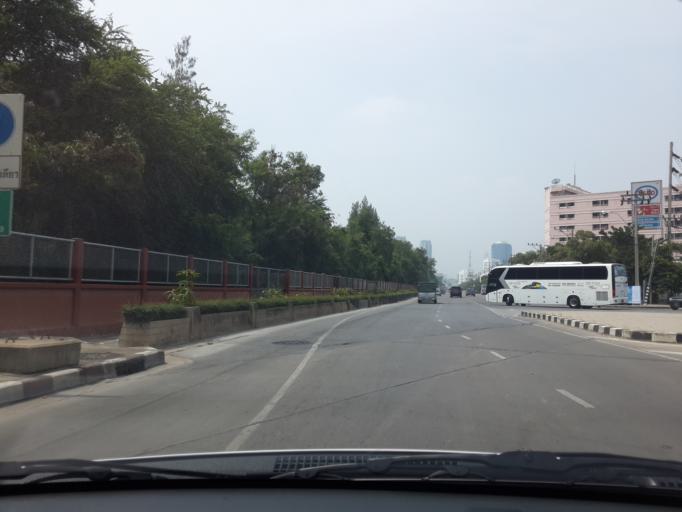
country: TH
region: Bangkok
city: Huai Khwang
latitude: 13.7664
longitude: 100.5845
